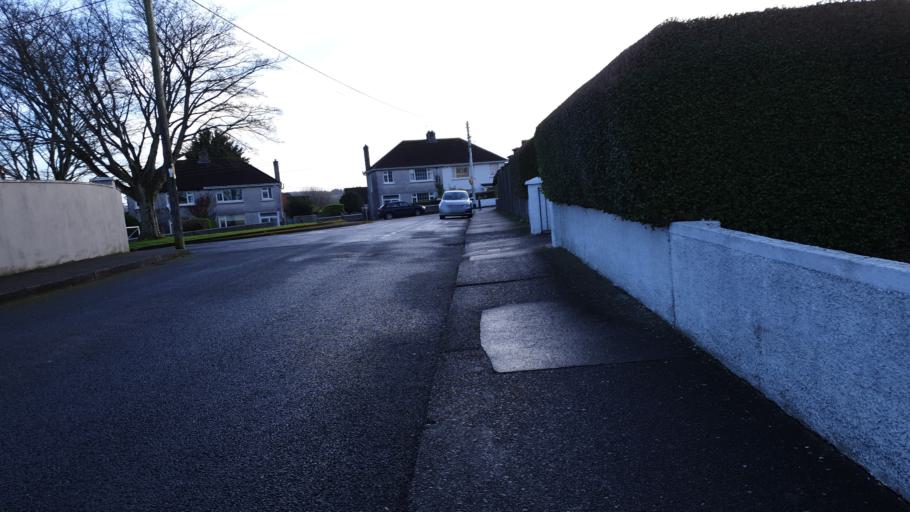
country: IE
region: Munster
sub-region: County Cork
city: Cork
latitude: 51.8895
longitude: -8.4270
